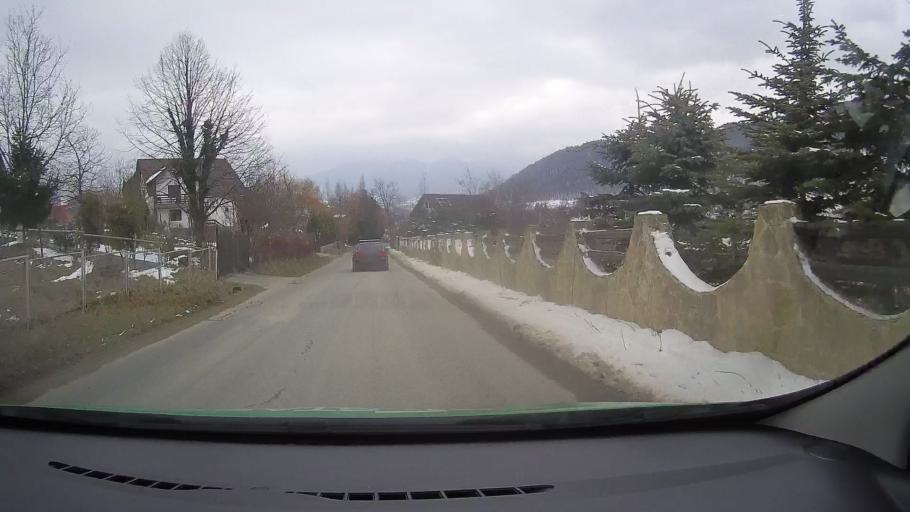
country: RO
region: Brasov
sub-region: Comuna Bran
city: Bran
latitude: 45.5325
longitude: 25.3466
